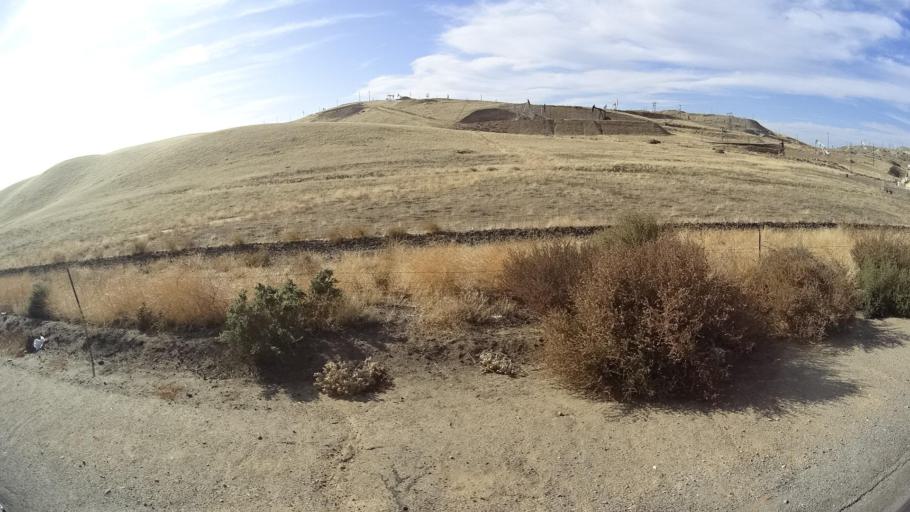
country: US
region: California
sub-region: Kern County
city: Oildale
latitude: 35.6100
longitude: -118.9667
